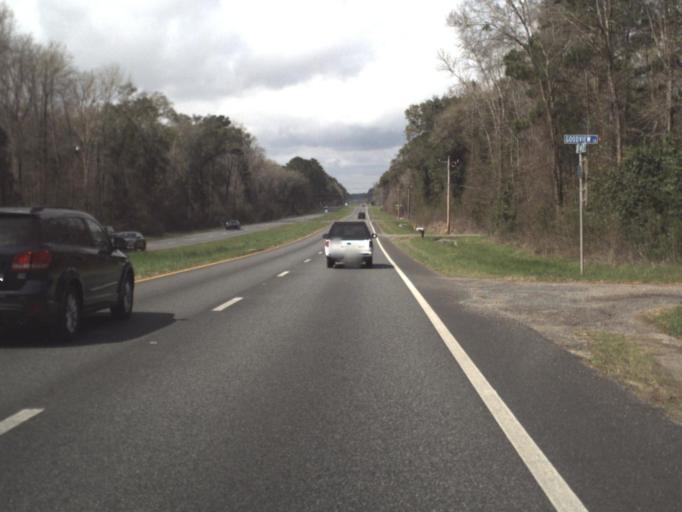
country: US
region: Florida
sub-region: Leon County
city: Tallahassee
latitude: 30.4207
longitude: -84.1617
